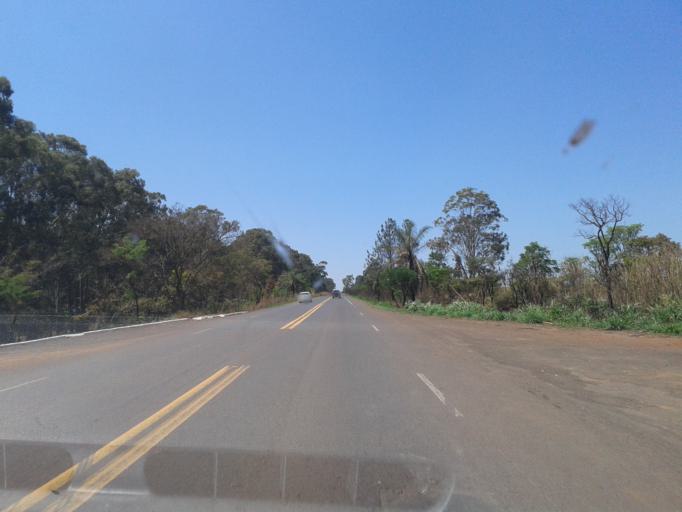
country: BR
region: Minas Gerais
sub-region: Araxa
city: Araxa
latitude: -19.3936
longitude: -47.3312
